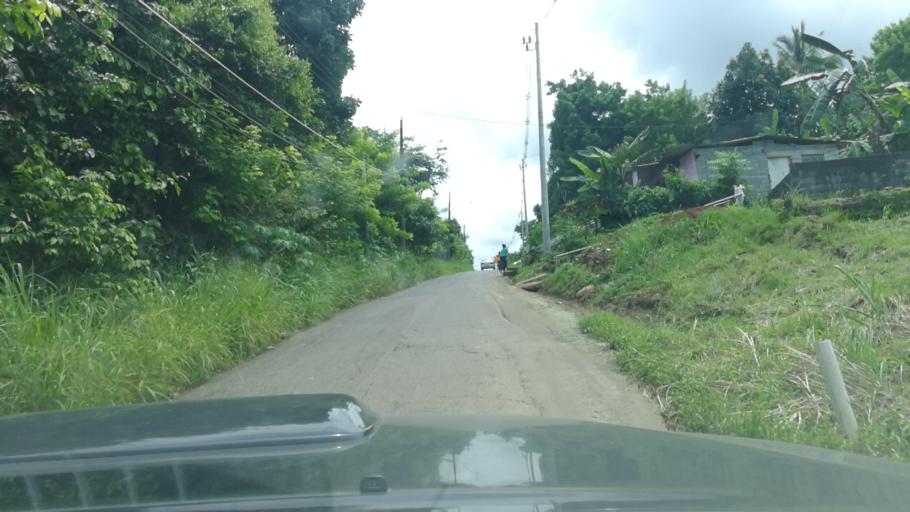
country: PA
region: Panama
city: San Miguelito
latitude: 9.0993
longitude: -79.4562
